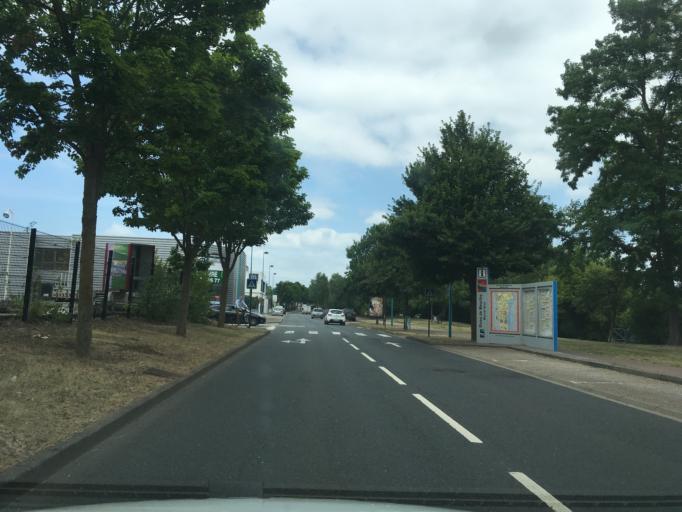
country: FR
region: Lorraine
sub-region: Departement de Meurthe-et-Moselle
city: Tomblaine
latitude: 48.6825
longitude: 6.2066
